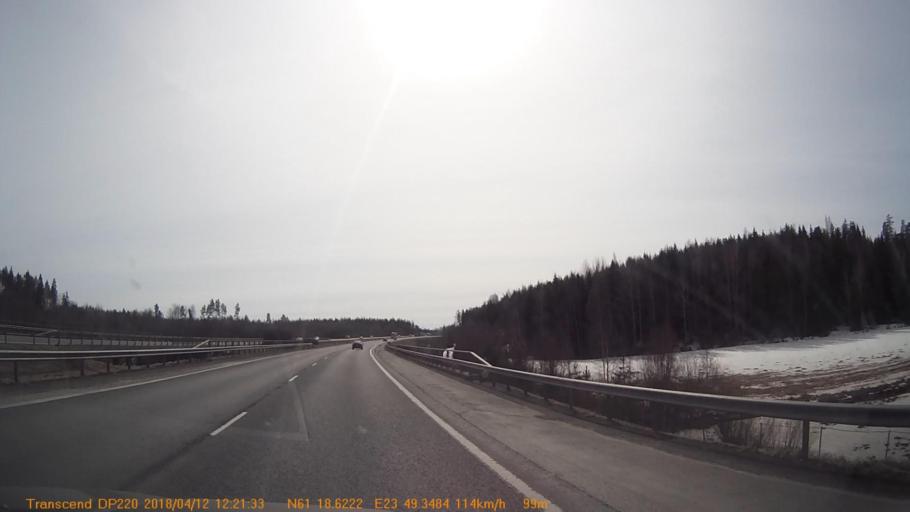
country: FI
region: Pirkanmaa
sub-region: Tampere
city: Lempaeaelae
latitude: 61.3098
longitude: 23.8227
